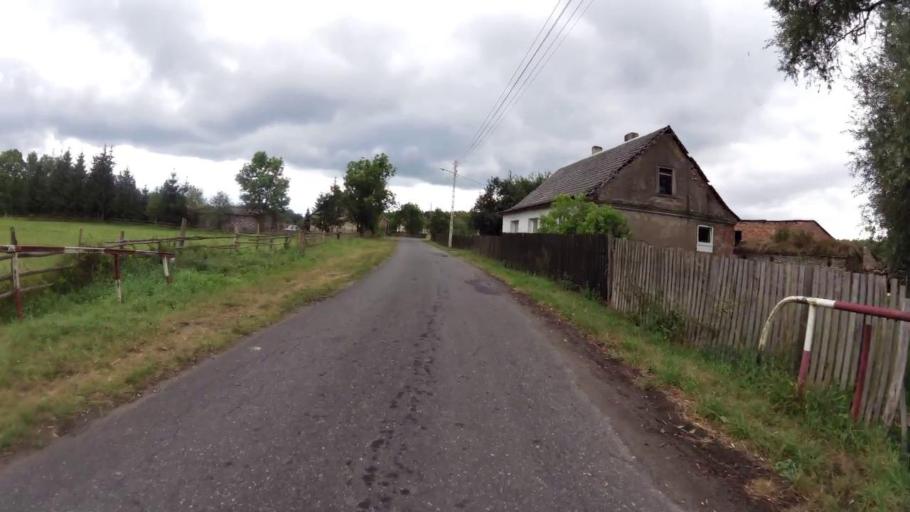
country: PL
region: West Pomeranian Voivodeship
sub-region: Powiat mysliborski
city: Debno
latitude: 52.8191
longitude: 14.7284
